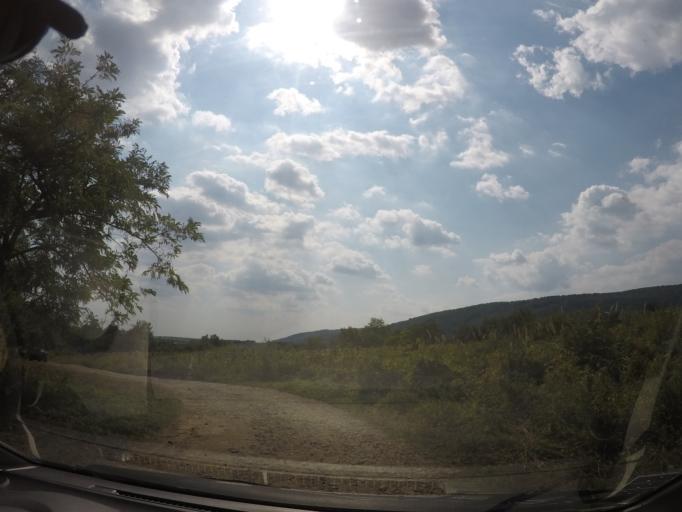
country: SK
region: Banskobystricky
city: Svaety Anton
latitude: 48.3056
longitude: 18.9581
